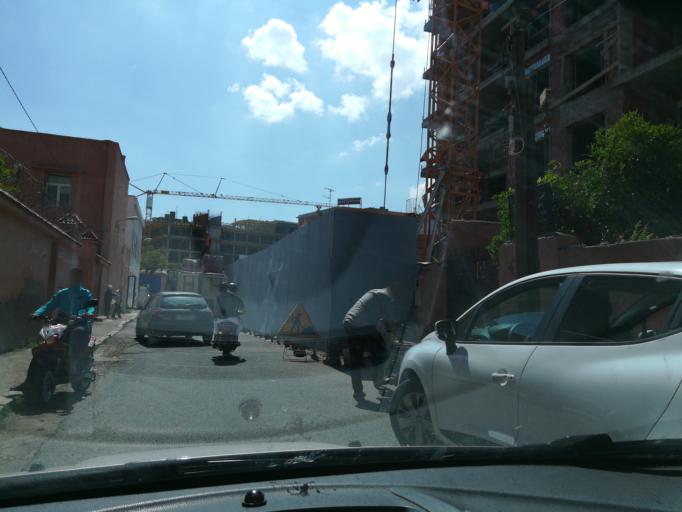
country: MA
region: Marrakech-Tensift-Al Haouz
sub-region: Marrakech
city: Marrakesh
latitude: 31.6341
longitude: -8.0056
